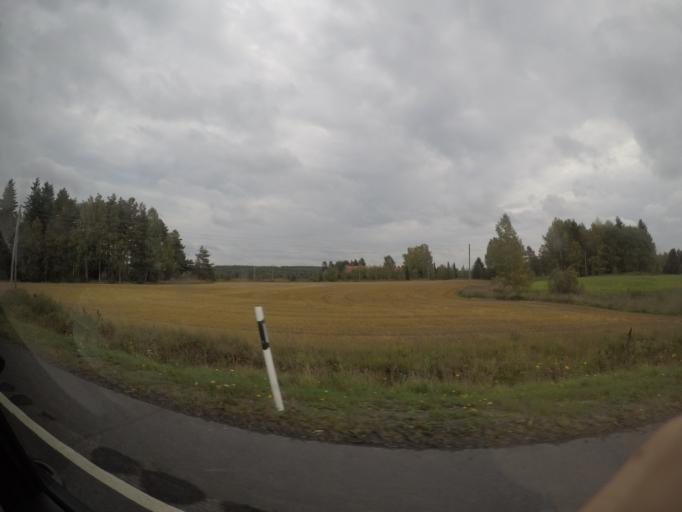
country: FI
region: Haeme
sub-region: Haemeenlinna
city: Parola
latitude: 61.1137
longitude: 24.4154
